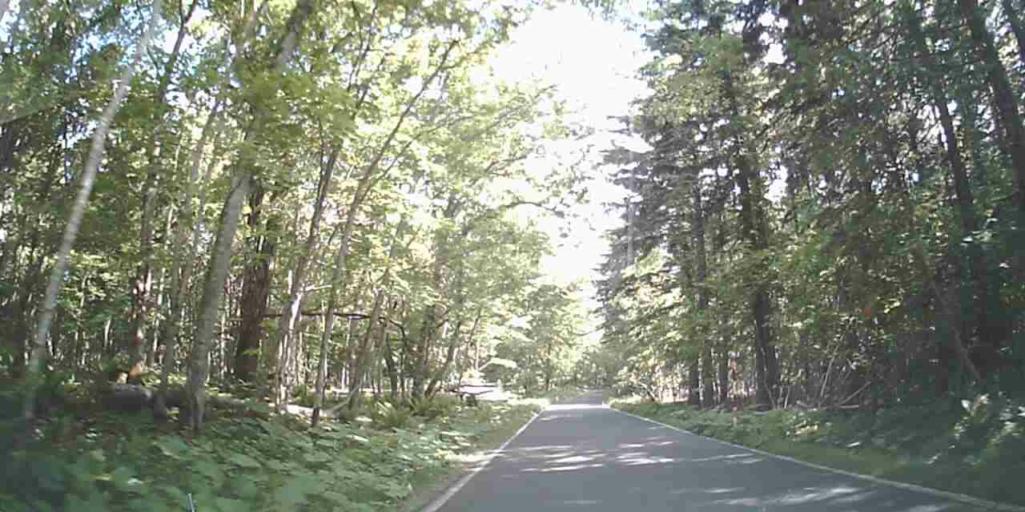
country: JP
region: Hokkaido
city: Shiraoi
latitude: 42.7354
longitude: 141.4106
